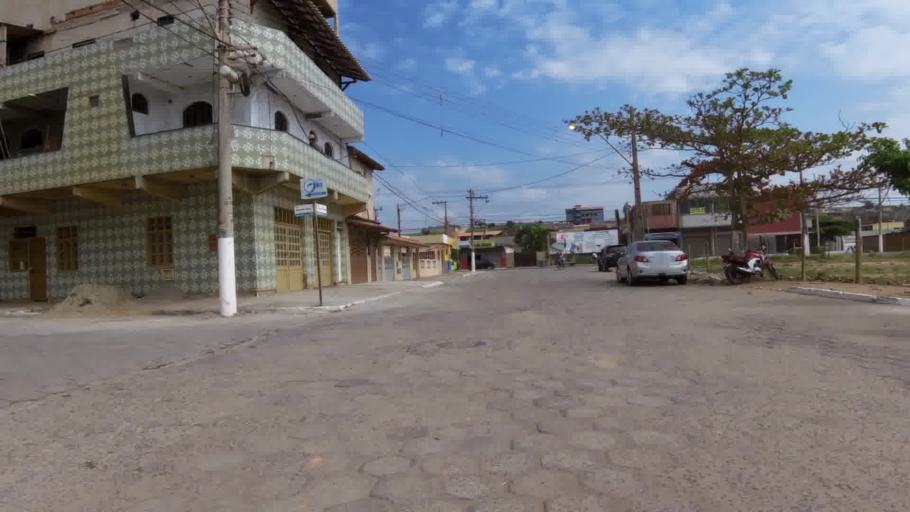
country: BR
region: Espirito Santo
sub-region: Marataizes
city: Marataizes
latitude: -21.0247
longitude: -40.8159
